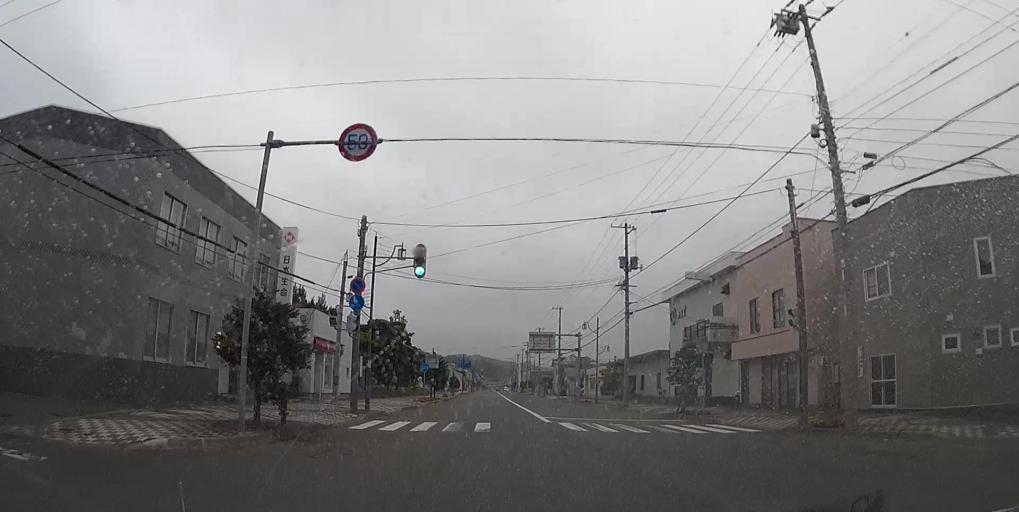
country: JP
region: Hokkaido
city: Iwanai
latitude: 42.4287
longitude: 140.0078
